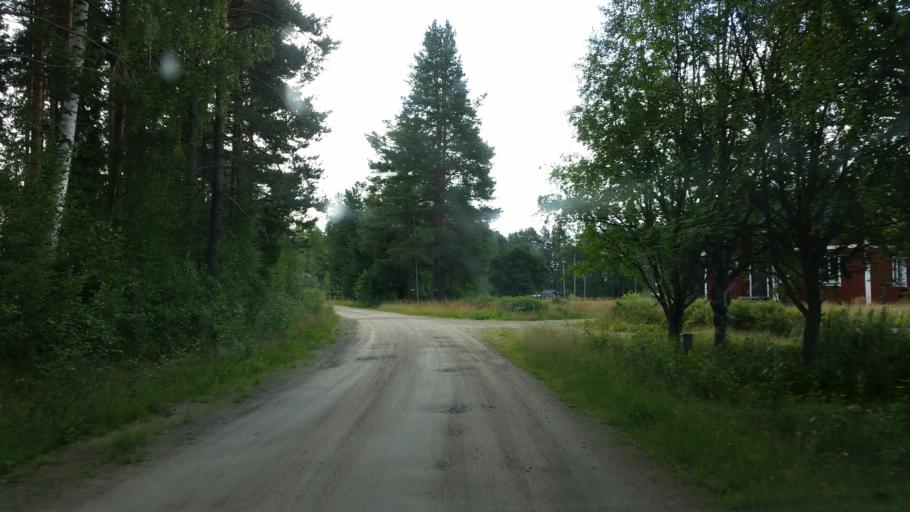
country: SE
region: Vaesternorrland
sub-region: Ange Kommun
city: Ange
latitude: 62.1875
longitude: 15.6449
